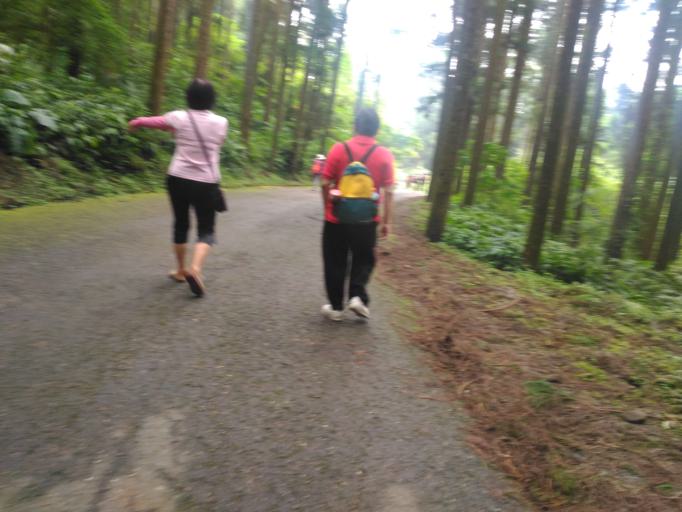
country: TW
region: Taiwan
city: Lugu
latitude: 23.6606
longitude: 120.7971
